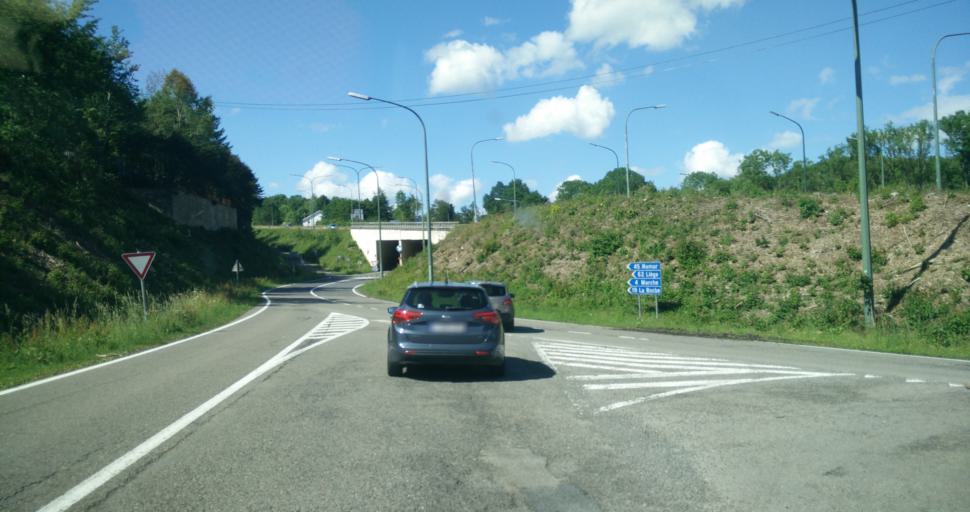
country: BE
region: Wallonia
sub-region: Province du Luxembourg
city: Marche-en-Famenne
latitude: 50.2047
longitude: 5.3674
